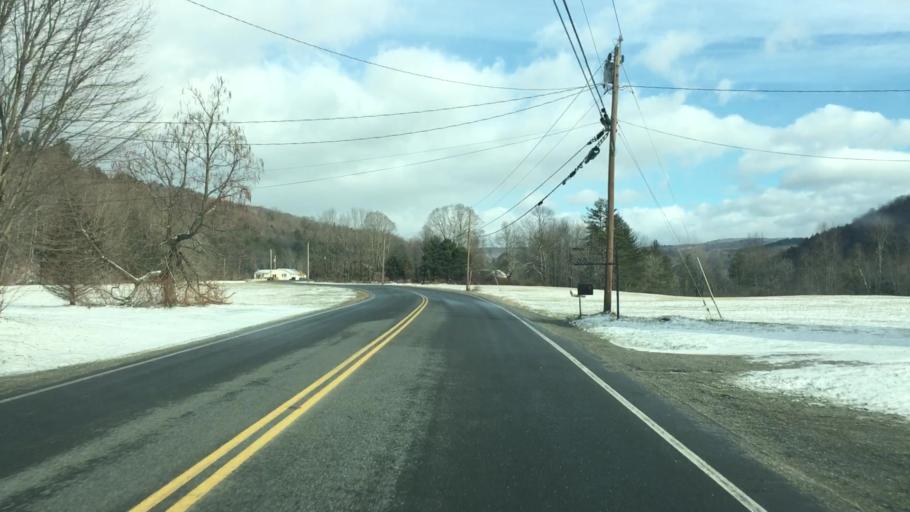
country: US
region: Massachusetts
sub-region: Franklin County
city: Colrain
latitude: 42.7061
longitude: -72.7005
